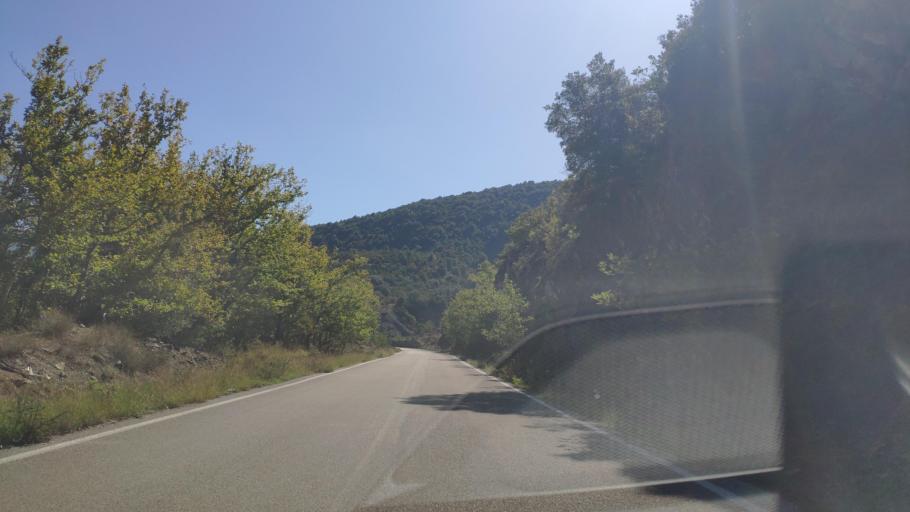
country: GR
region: West Greece
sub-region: Nomos Aitolias kai Akarnanias
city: Sardinia
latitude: 38.9223
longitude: 21.3634
